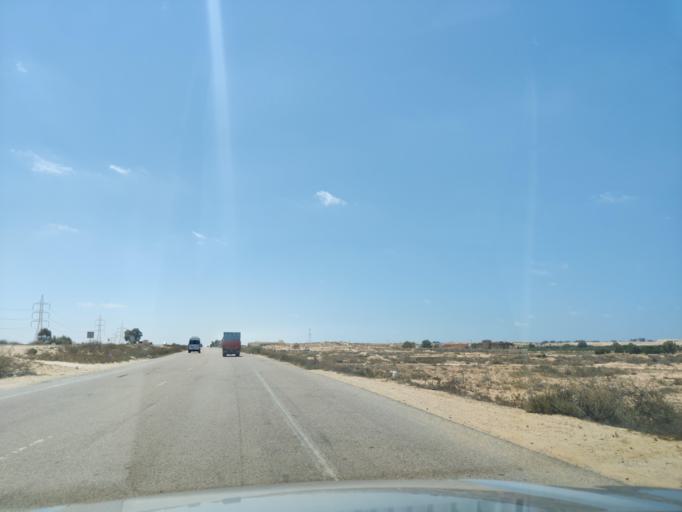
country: EG
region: Muhafazat Matruh
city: Al `Alamayn
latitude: 31.0702
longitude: 28.1585
